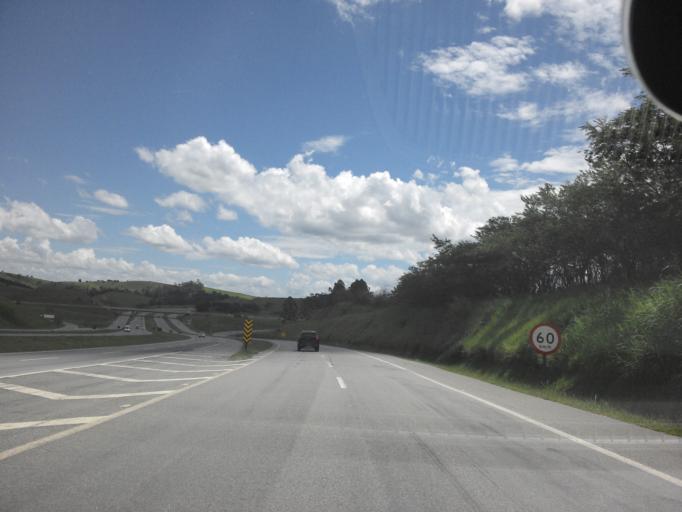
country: BR
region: Sao Paulo
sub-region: Jacarei
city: Jacarei
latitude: -23.3440
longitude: -46.0133
